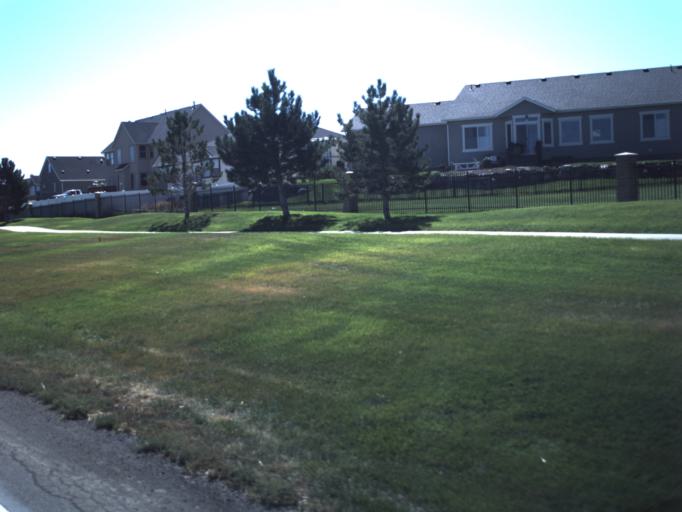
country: US
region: Utah
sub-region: Utah County
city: Saratoga Springs
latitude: 40.3181
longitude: -111.8985
